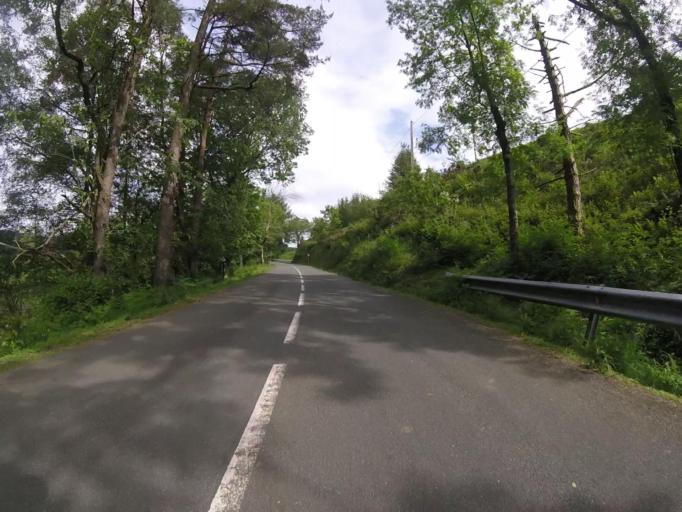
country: ES
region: Navarre
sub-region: Provincia de Navarra
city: Arano
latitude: 43.2479
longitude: -1.8475
